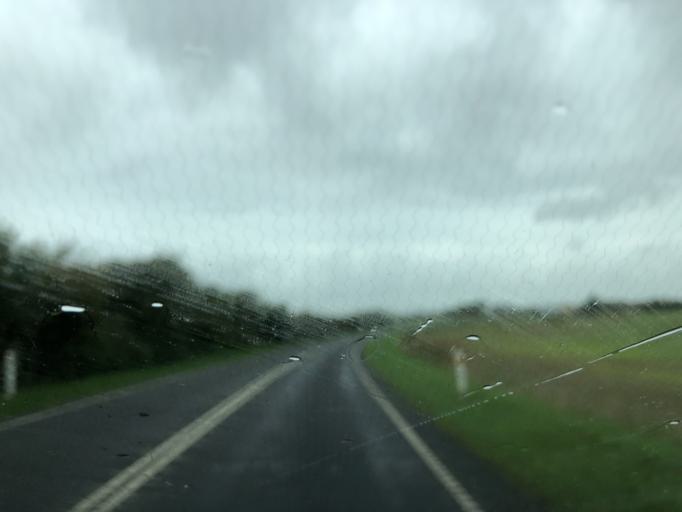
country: DK
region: North Denmark
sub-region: Thisted Kommune
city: Hurup
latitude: 56.7374
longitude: 8.3328
